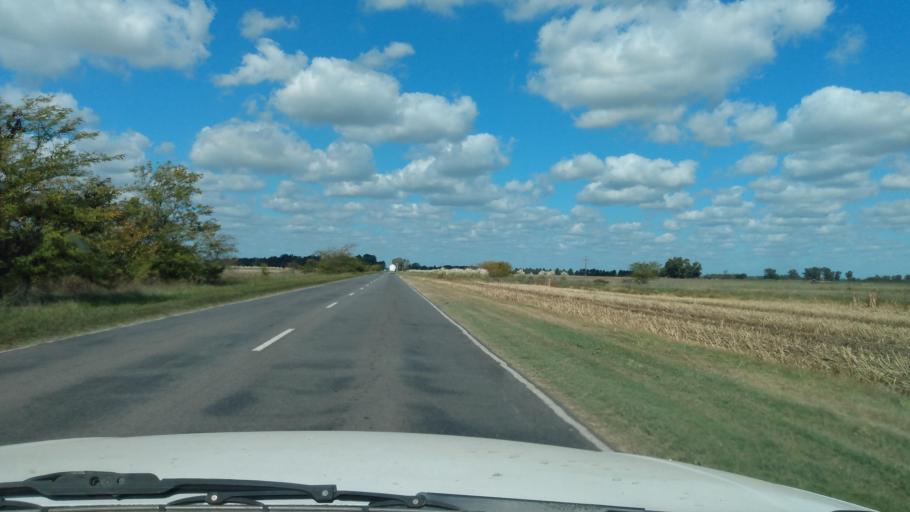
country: AR
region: Buenos Aires
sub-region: Partido de Navarro
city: Navarro
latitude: -34.9786
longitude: -59.3165
